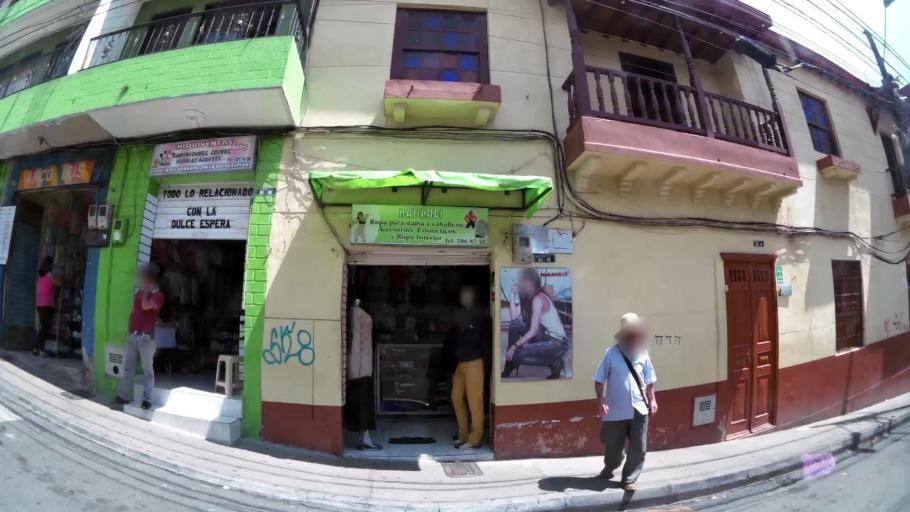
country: CO
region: Antioquia
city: La Estrella
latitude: 6.1843
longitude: -75.6581
